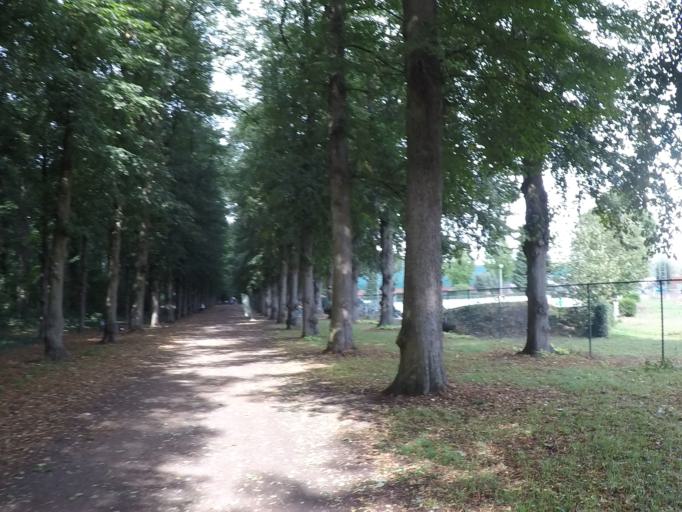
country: BE
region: Flanders
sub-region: Provincie Antwerpen
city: Vorselaar
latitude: 51.2050
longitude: 4.7729
